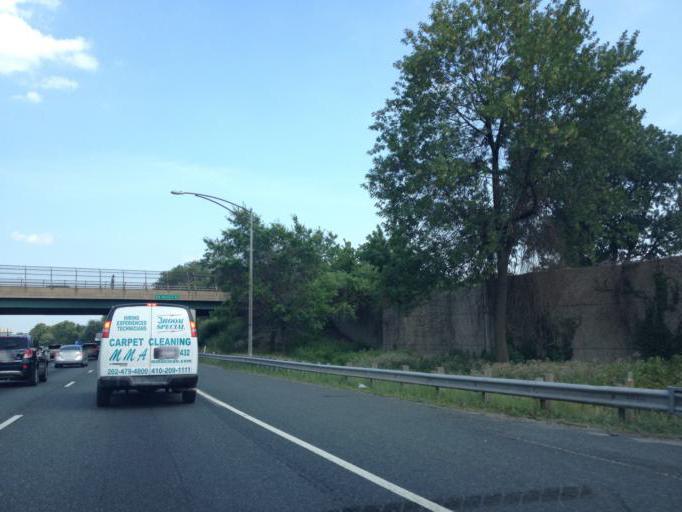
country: US
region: Maryland
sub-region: Baltimore County
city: Parkville
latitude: 39.3936
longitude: -76.5435
